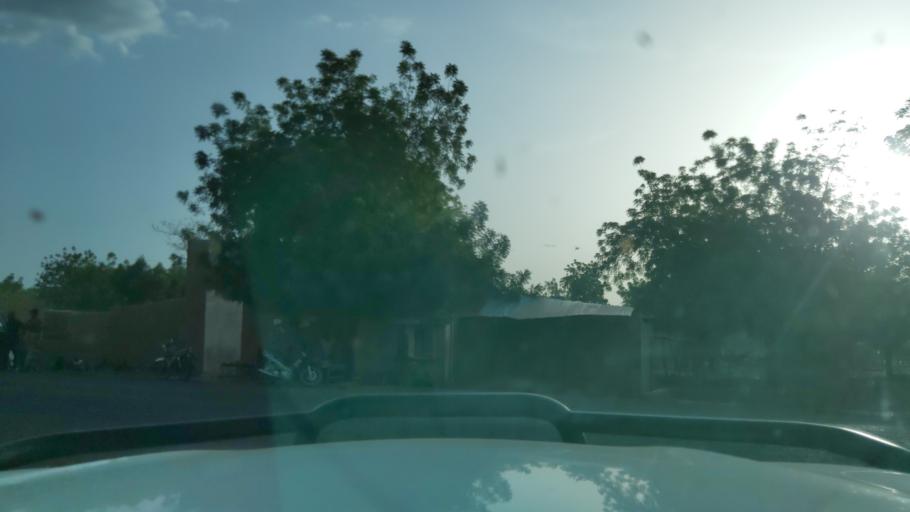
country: ML
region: Koulikoro
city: Kolokani
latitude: 13.2031
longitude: -7.9313
